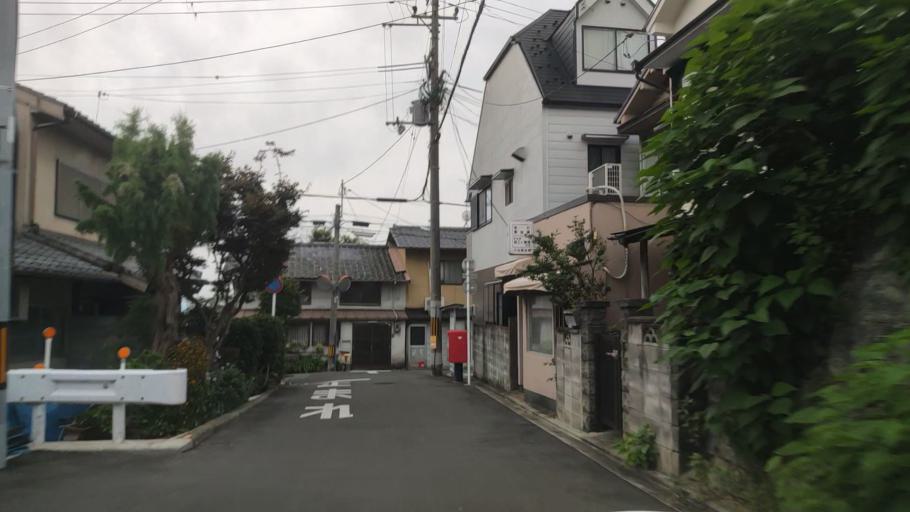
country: JP
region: Kyoto
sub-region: Kyoto-shi
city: Kamigyo-ku
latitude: 35.0213
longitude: 135.7859
